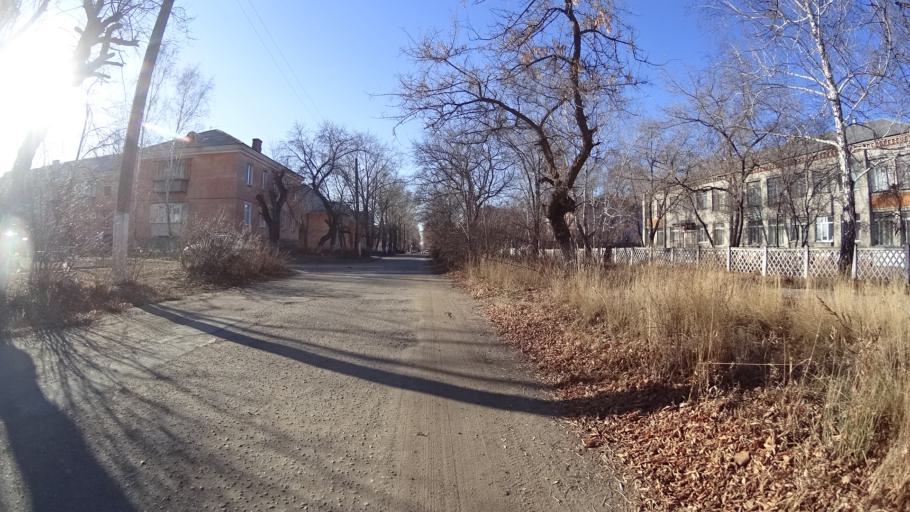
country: RU
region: Chelyabinsk
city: Troitsk
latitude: 54.0456
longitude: 61.6341
